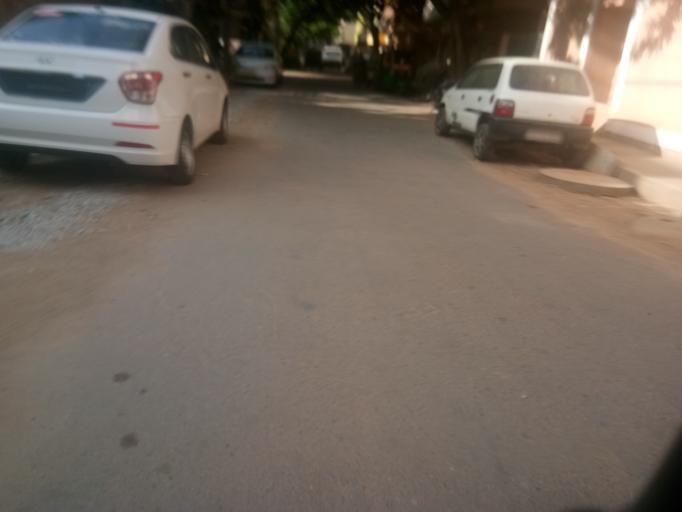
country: IN
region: Karnataka
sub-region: Bangalore Urban
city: Bangalore
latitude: 13.0059
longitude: 77.6010
